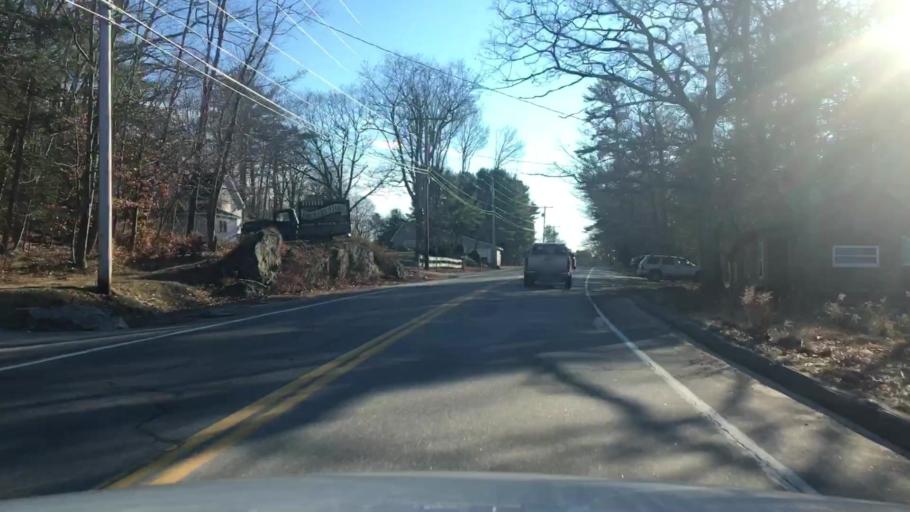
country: US
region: Maine
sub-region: Cumberland County
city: Brunswick
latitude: 43.8622
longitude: -69.9135
